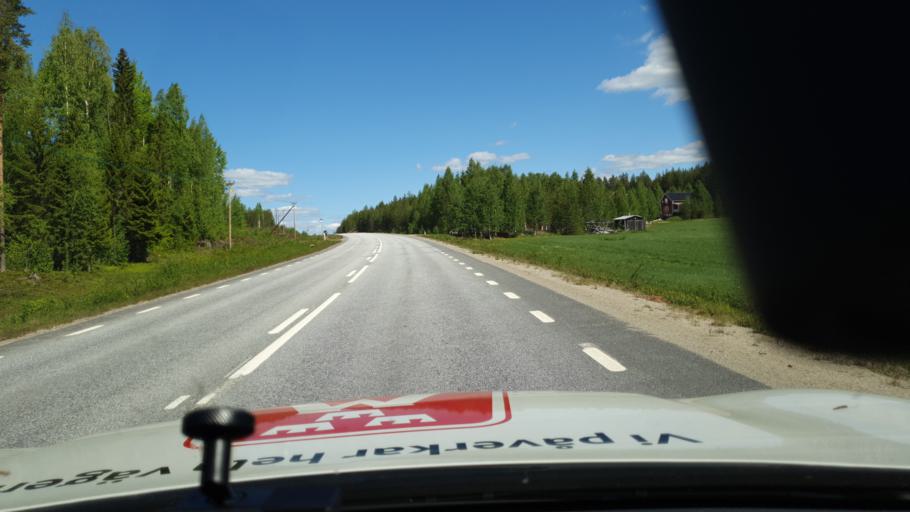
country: SE
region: Vaesterbotten
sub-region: Vannas Kommun
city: Vaennaes
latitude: 64.0266
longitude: 19.6935
